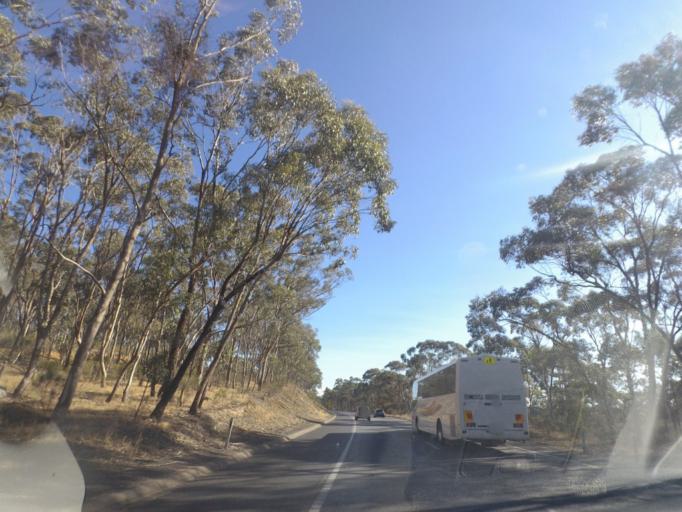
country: AU
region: Victoria
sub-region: Murrindindi
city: Kinglake West
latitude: -37.1782
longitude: 145.0705
